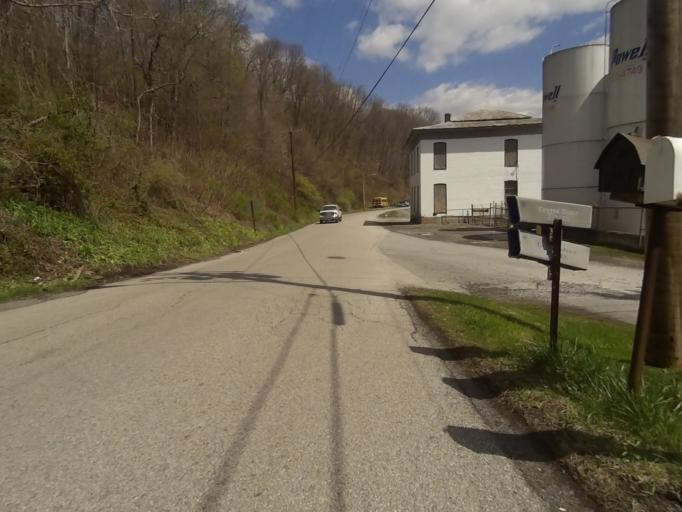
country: US
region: Pennsylvania
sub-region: Centre County
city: Bellefonte
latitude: 40.9089
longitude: -77.7861
